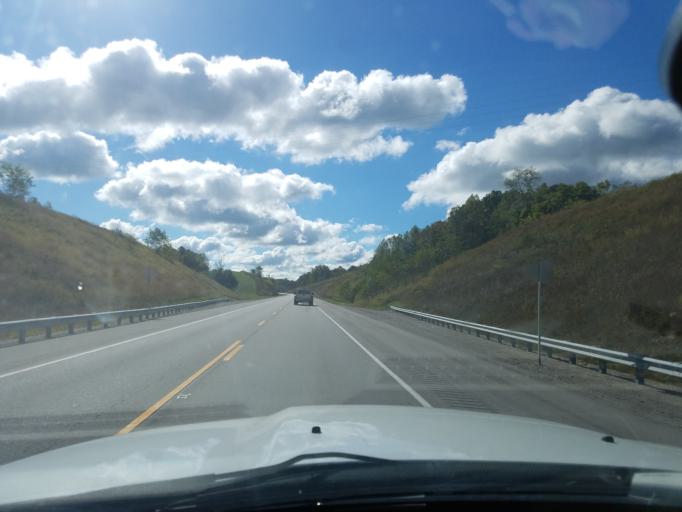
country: US
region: Kentucky
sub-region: Rockcastle County
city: Brodhead
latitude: 37.3675
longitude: -84.4115
